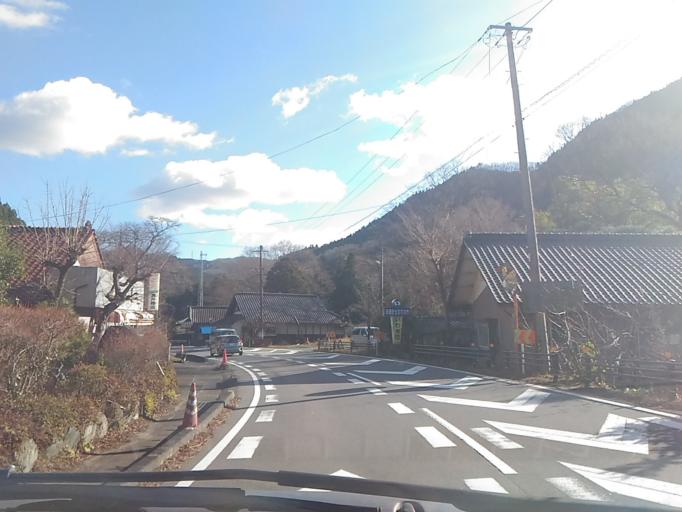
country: JP
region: Fukushima
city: Ishikawa
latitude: 37.0357
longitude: 140.6241
